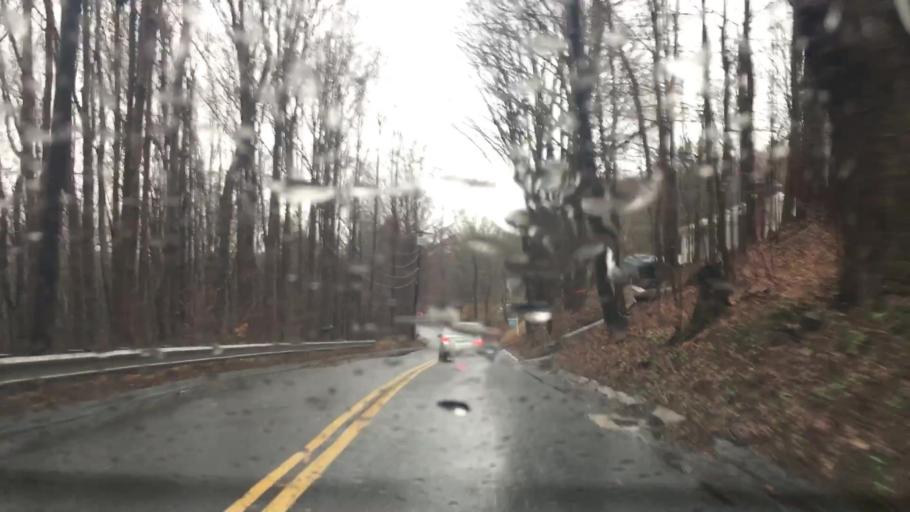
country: US
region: Connecticut
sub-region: Fairfield County
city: Danbury
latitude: 41.4254
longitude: -73.4644
